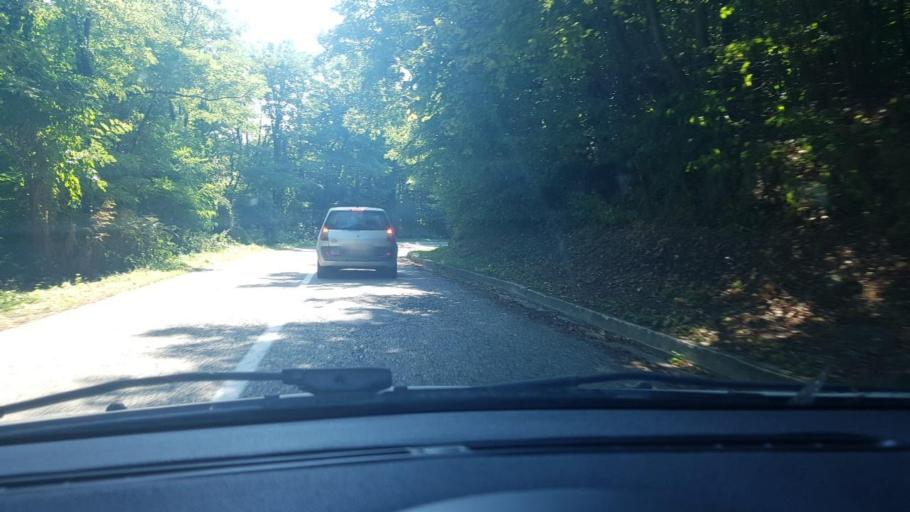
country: HR
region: Krapinsko-Zagorska
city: Marija Bistrica
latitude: 45.9585
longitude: 16.1459
